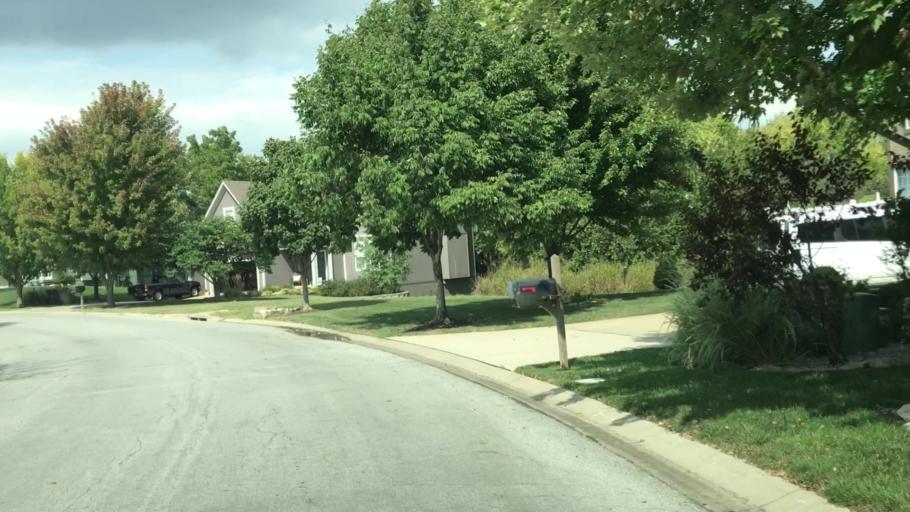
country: US
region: Kansas
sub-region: Johnson County
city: Olathe
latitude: 38.9557
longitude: -94.8355
